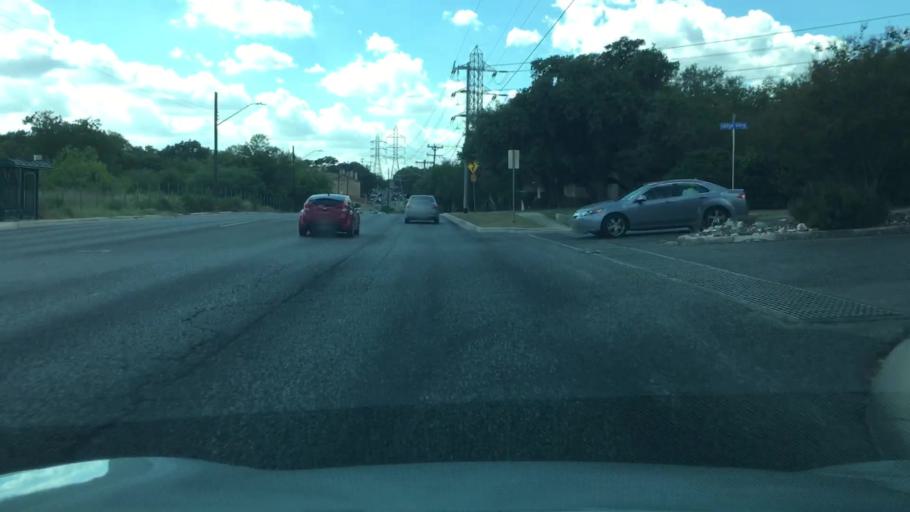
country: US
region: Texas
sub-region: Bexar County
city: Hollywood Park
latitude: 29.5902
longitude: -98.4608
